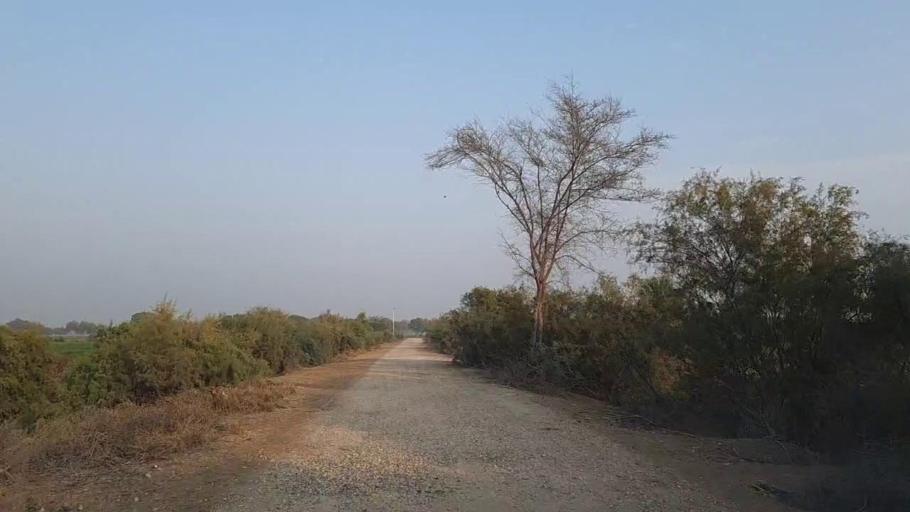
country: PK
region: Sindh
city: Jam Sahib
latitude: 26.3204
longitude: 68.5970
